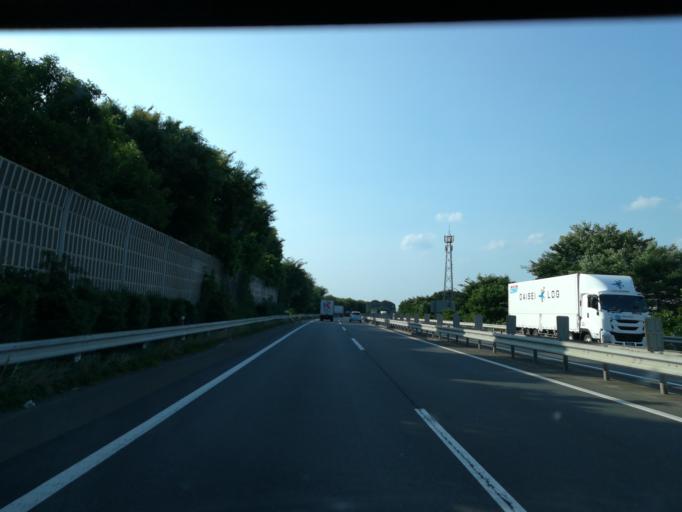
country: JP
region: Saitama
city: Sayama
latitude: 35.8710
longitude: 139.3762
